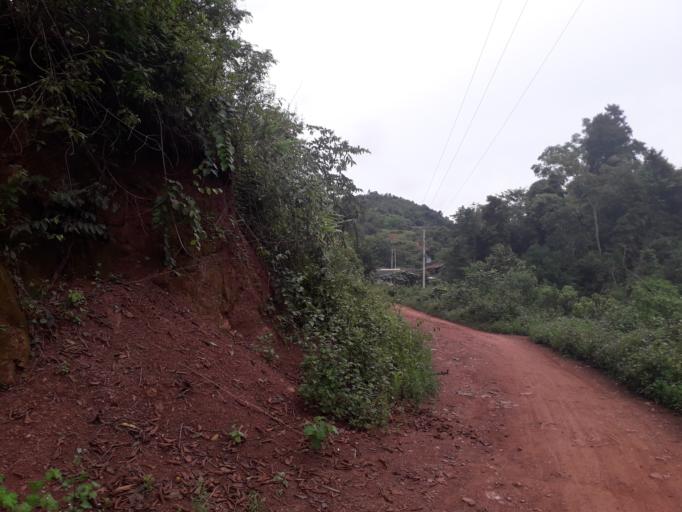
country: CN
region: Yunnan
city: Menglie
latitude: 22.2160
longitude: 101.6557
